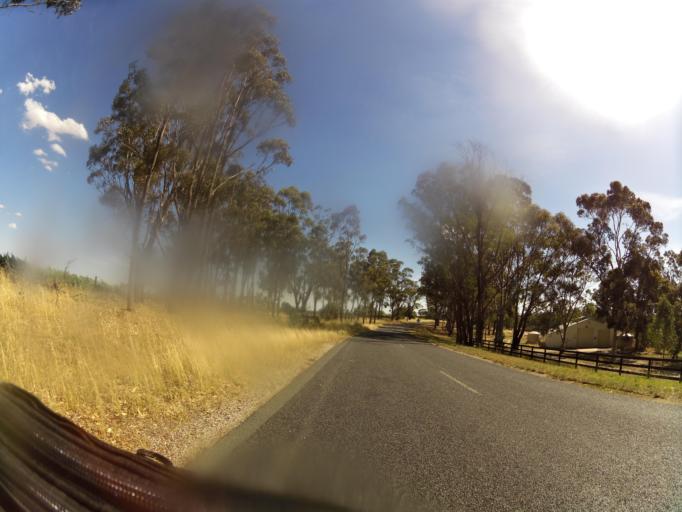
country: AU
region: Victoria
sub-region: Campaspe
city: Kyabram
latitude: -36.8556
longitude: 145.0968
